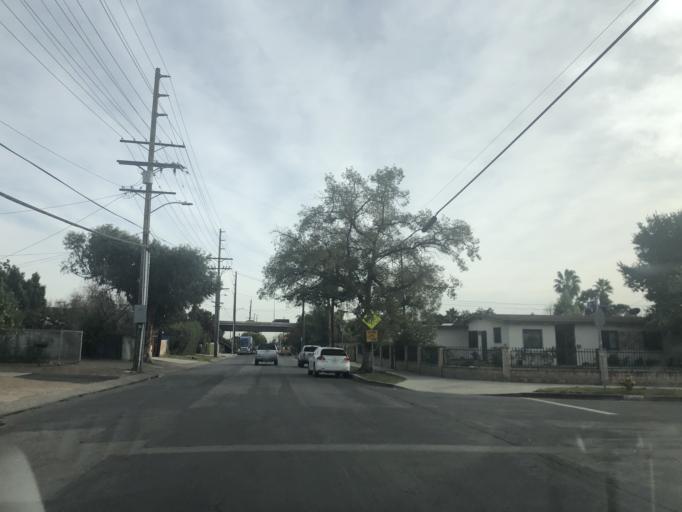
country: US
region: California
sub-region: Los Angeles County
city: San Fernando
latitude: 34.2711
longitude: -118.4335
